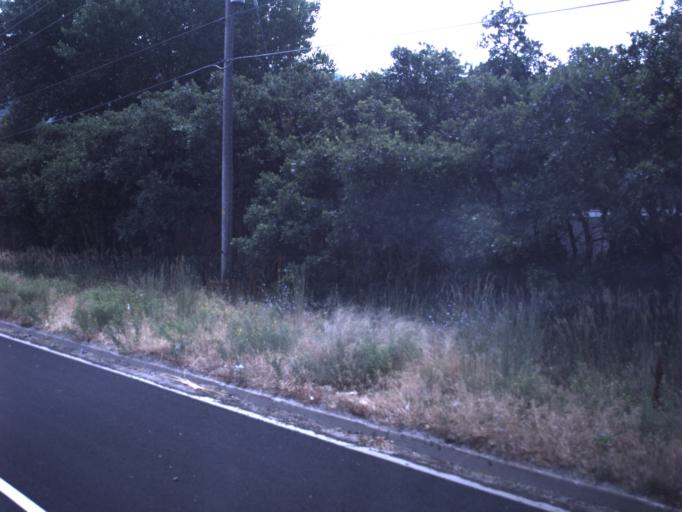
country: US
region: Utah
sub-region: Davis County
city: South Weber
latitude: 41.1019
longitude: -111.9321
